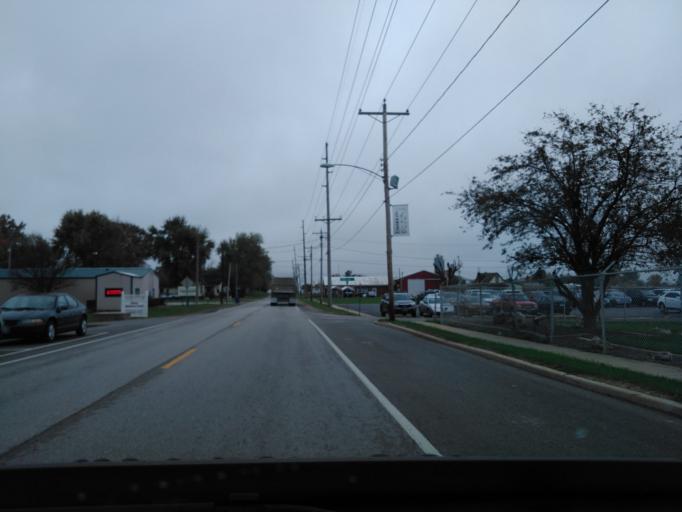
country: US
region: Illinois
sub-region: Bond County
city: Greenville
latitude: 38.8831
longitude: -89.4144
